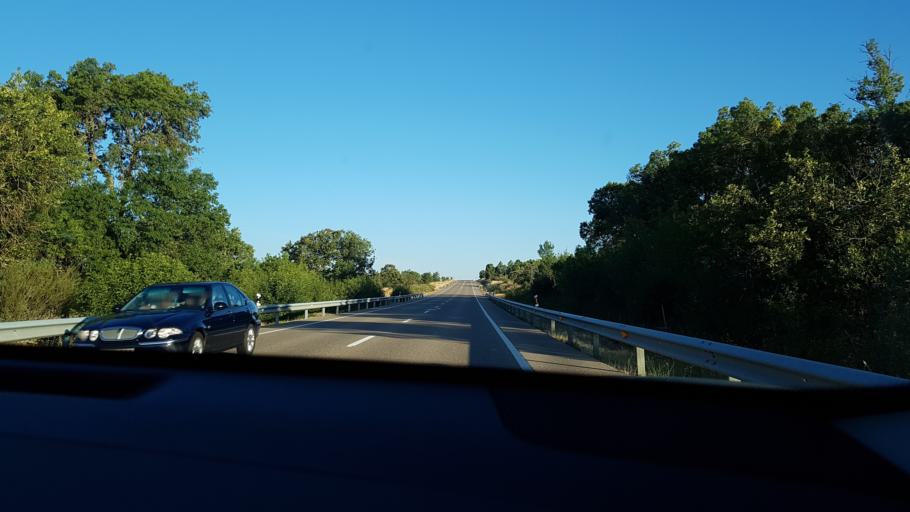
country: ES
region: Castille and Leon
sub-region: Provincia de Zamora
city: Samir de los Canos
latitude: 41.6486
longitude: -6.1674
